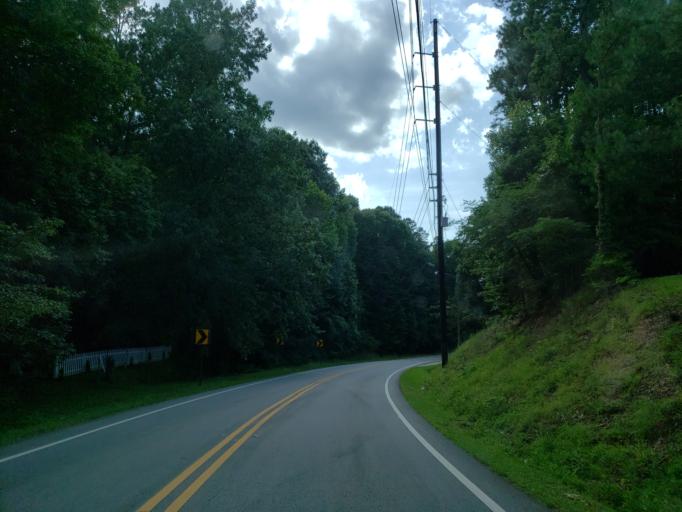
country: US
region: Georgia
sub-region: Cobb County
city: Powder Springs
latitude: 33.8738
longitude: -84.6406
